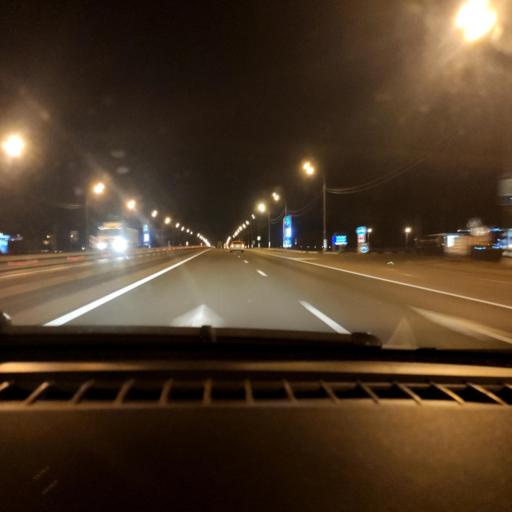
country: RU
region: Lipetsk
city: Khlevnoye
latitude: 52.2300
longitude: 39.0929
